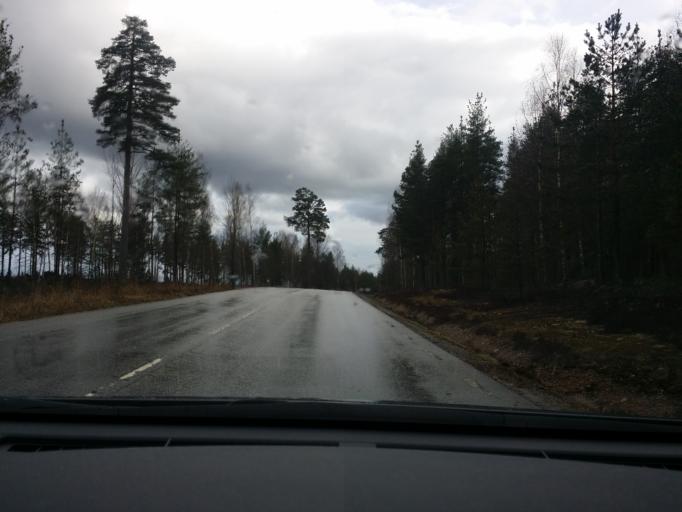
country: SE
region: Soedermanland
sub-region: Eskilstuna Kommun
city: Arla
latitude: 59.3415
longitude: 16.6914
